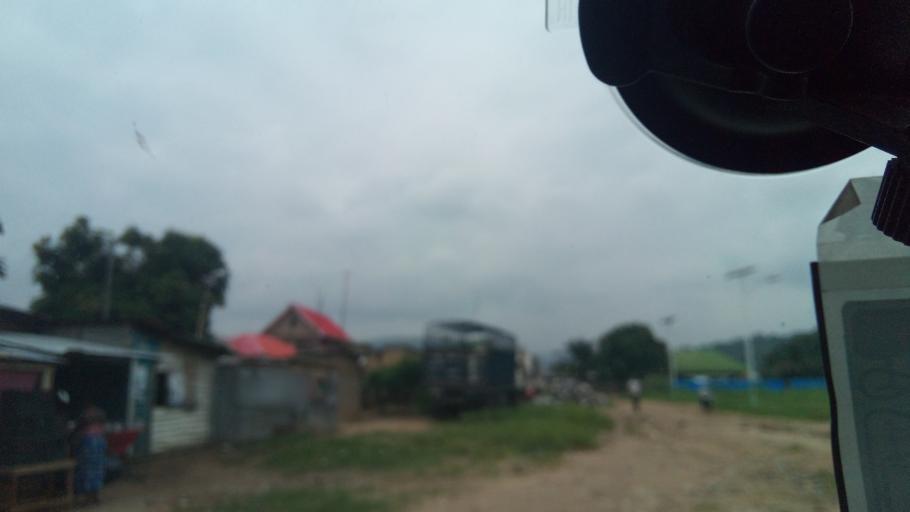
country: CG
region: Brazzaville
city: Brazzaville
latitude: -4.0554
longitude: 15.5555
